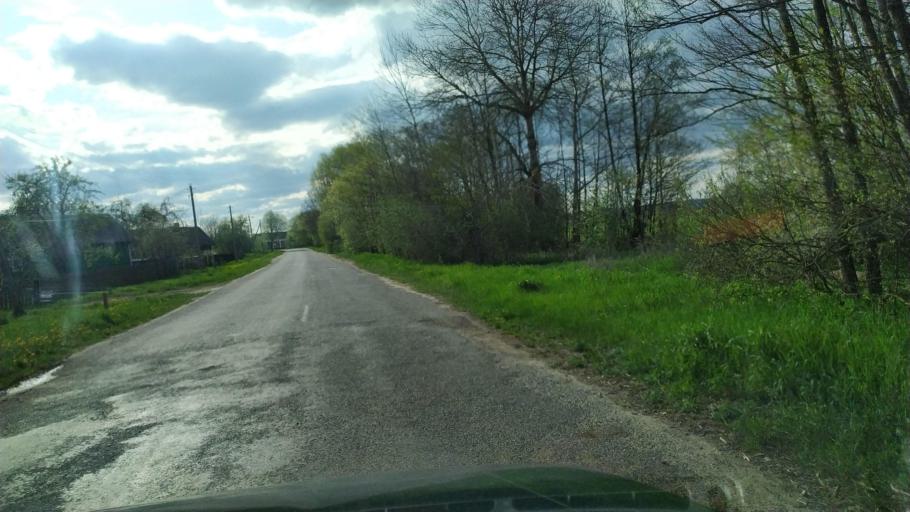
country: BY
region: Brest
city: Pruzhany
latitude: 52.7018
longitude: 24.1908
